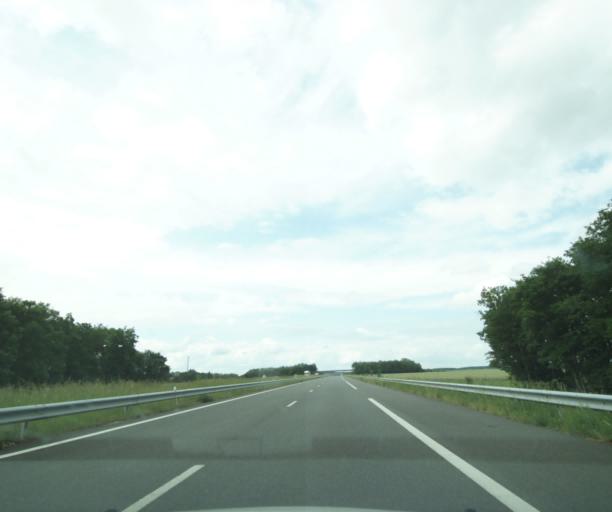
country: FR
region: Centre
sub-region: Departement du Cher
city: Levet
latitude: 46.8903
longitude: 2.4185
